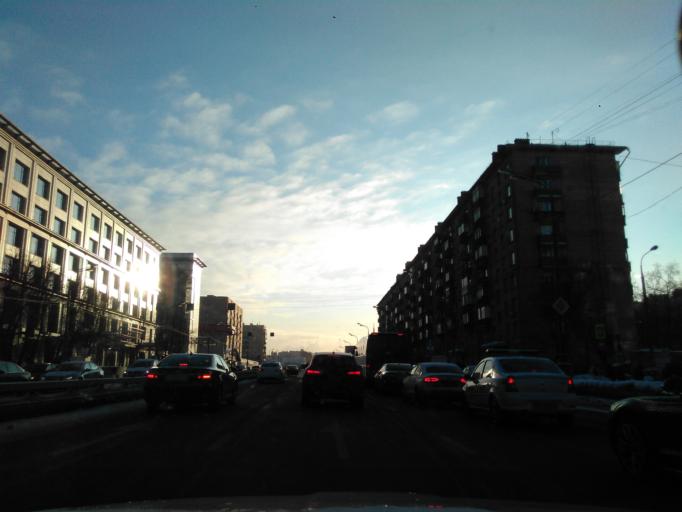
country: RU
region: Moskovskaya
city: Presnenskiy
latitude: 55.7641
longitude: 37.5545
